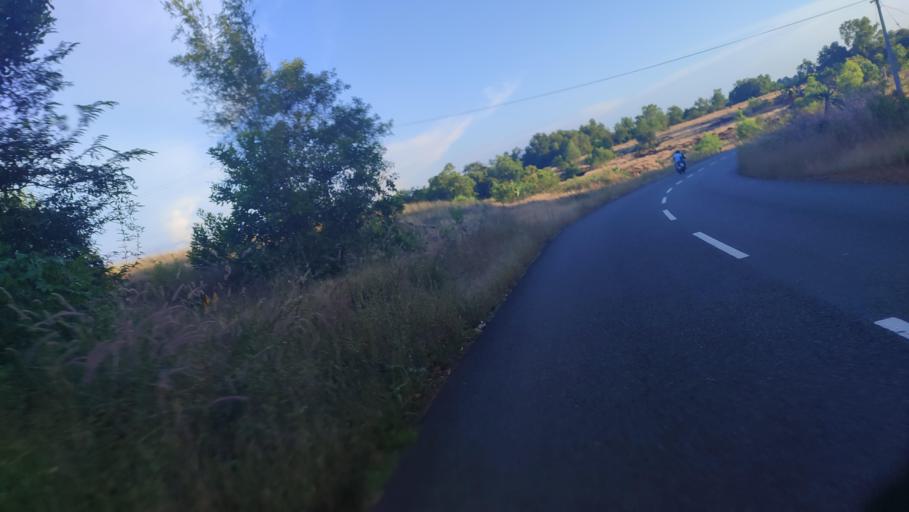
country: IN
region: Kerala
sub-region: Kasaragod District
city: Kasaragod
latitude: 12.4468
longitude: 75.0992
